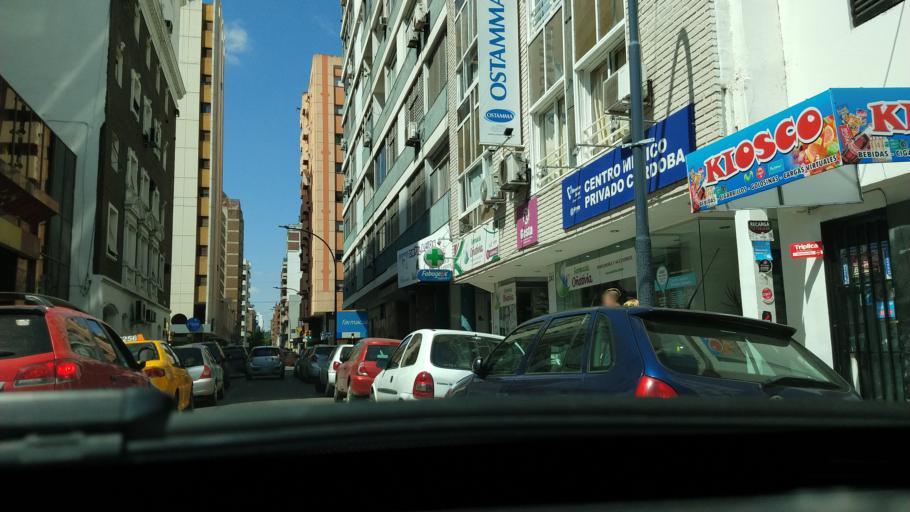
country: AR
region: Cordoba
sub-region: Departamento de Capital
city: Cordoba
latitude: -31.4099
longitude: -64.1937
